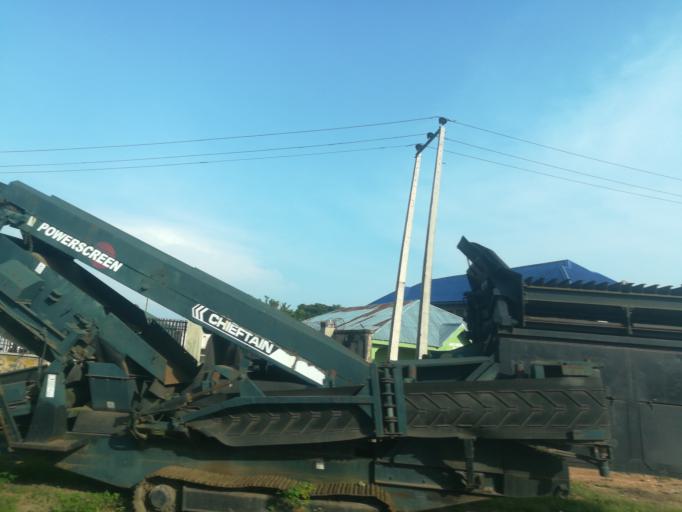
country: NG
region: Oyo
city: Moniya
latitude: 7.5135
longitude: 3.9128
